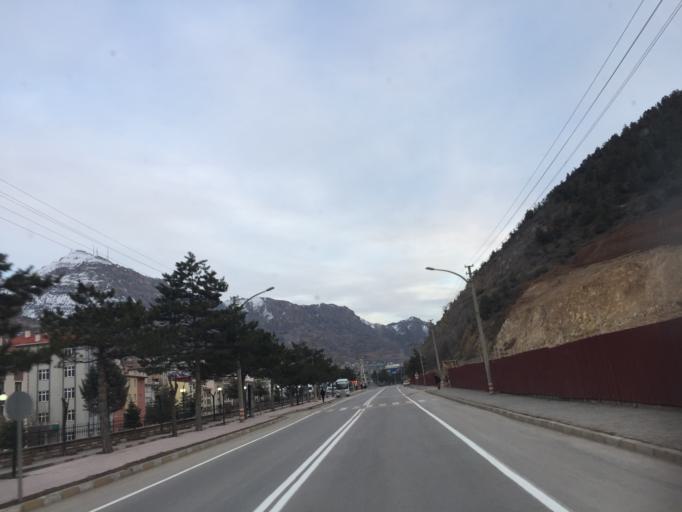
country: TR
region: Gumushane
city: Gumushkhane
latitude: 40.4613
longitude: 39.4695
